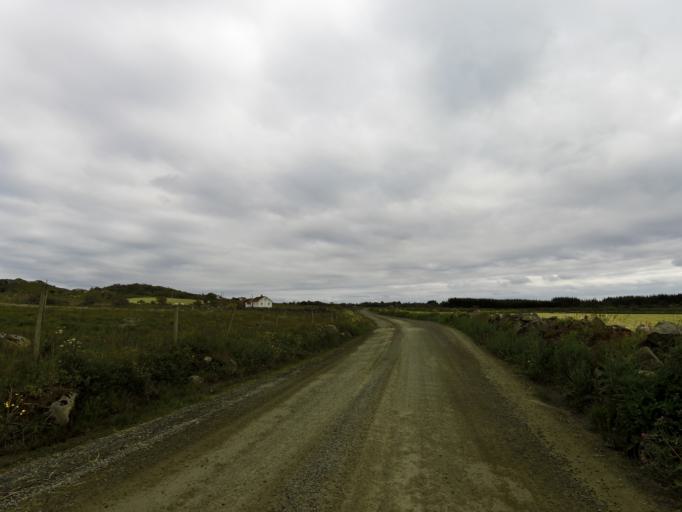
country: NO
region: Vest-Agder
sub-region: Farsund
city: Vestbygd
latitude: 58.1348
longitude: 6.6074
